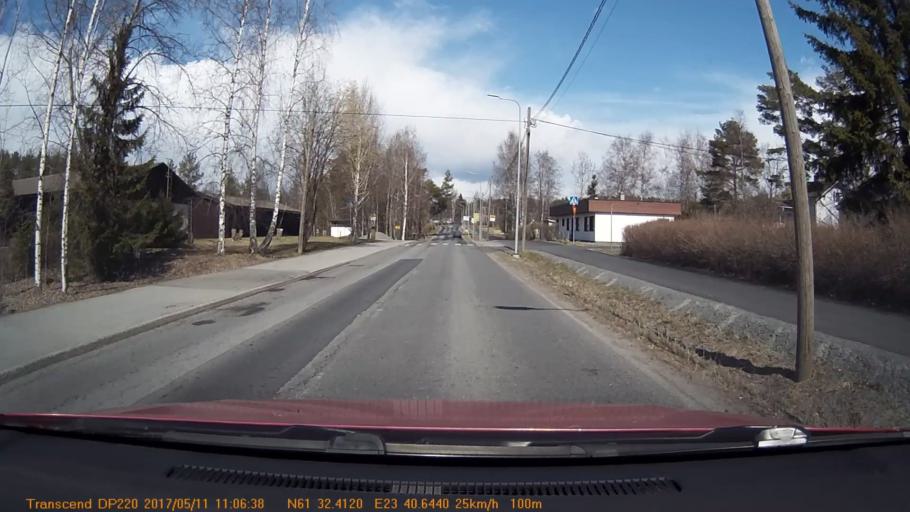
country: FI
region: Pirkanmaa
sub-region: Tampere
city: Yloejaervi
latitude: 61.5402
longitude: 23.6774
